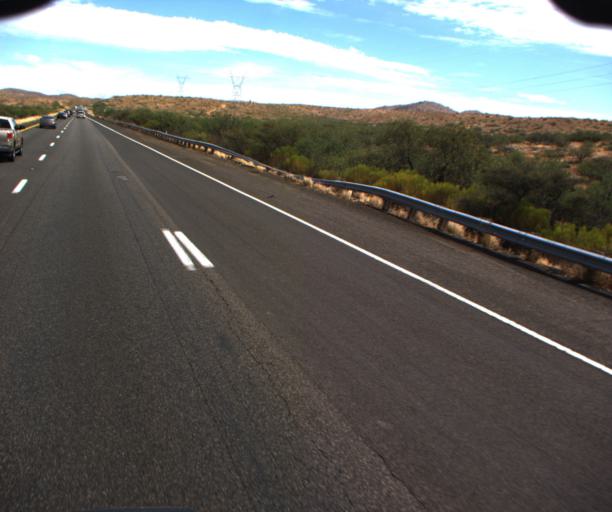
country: US
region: Arizona
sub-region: Yavapai County
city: Cordes Lakes
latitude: 34.2415
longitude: -112.1118
